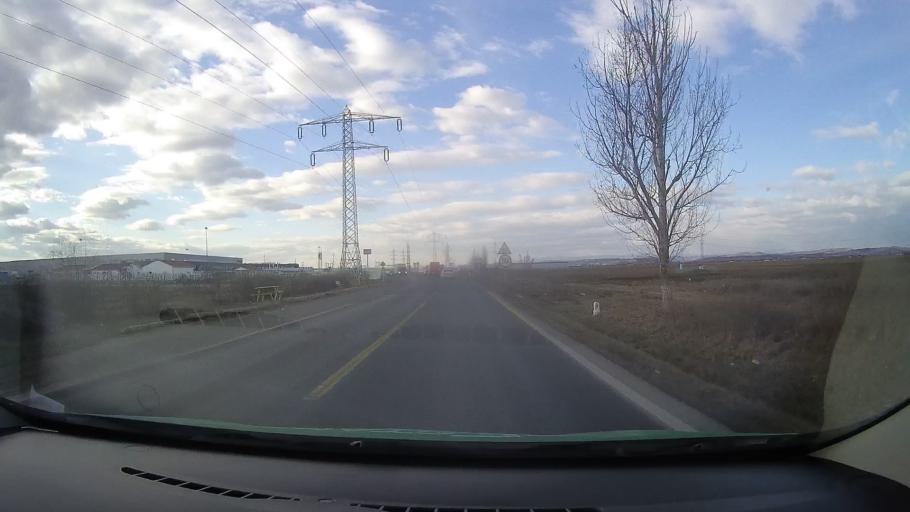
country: RO
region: Dambovita
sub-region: Comuna Comisani
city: Lazuri
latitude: 44.8743
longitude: 25.5207
